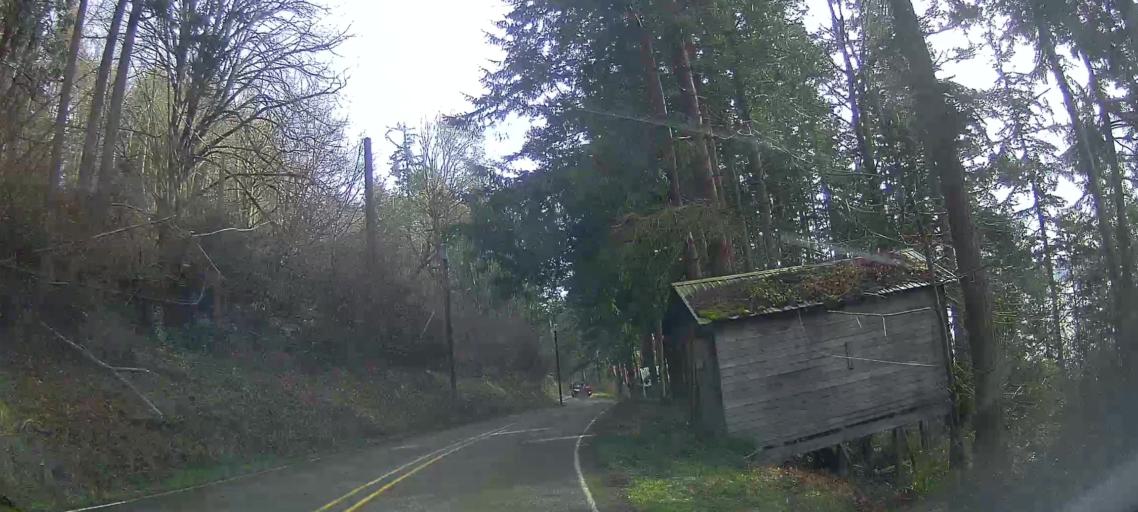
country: US
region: Washington
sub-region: Island County
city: Langley
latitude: 48.0629
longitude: -122.3817
